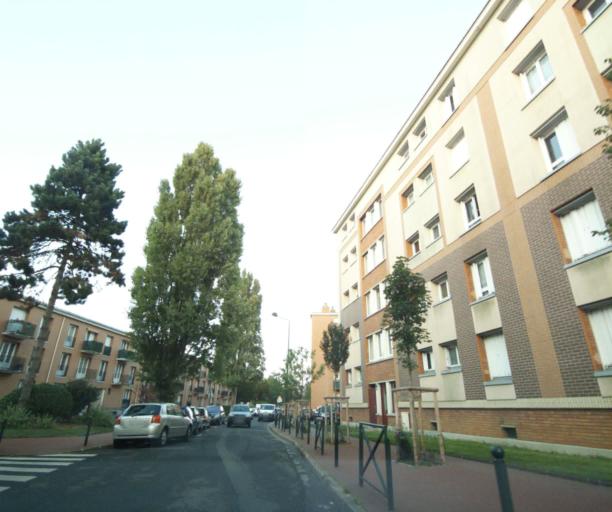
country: FR
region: Ile-de-France
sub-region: Departement des Hauts-de-Seine
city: Le Plessis-Robinson
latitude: 48.7860
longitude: 2.2441
